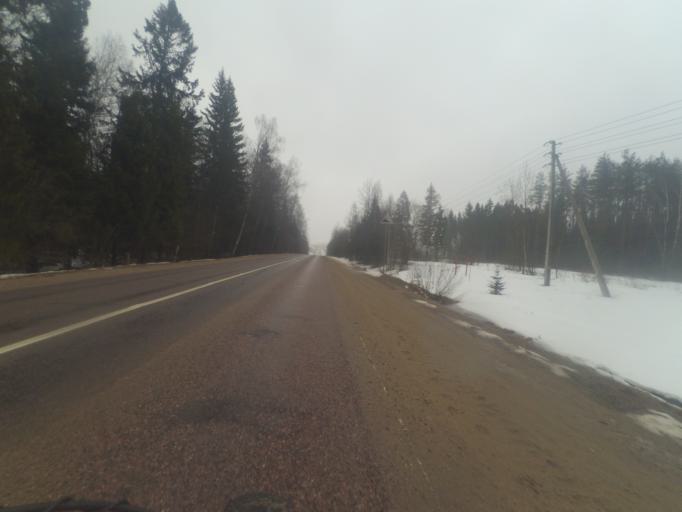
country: RU
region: Moskovskaya
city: Avtopoligon
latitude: 56.2660
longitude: 37.3251
